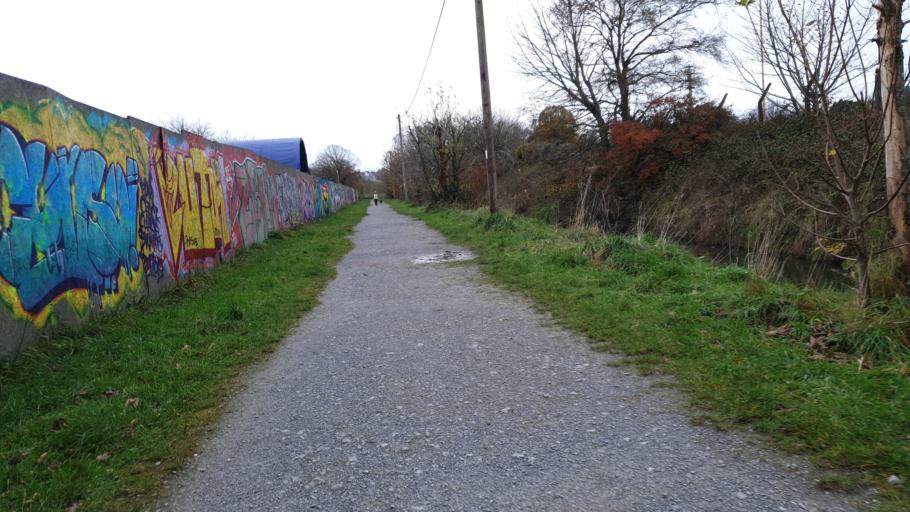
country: IE
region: Munster
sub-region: County Cork
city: Cork
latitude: 51.8989
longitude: -8.4398
